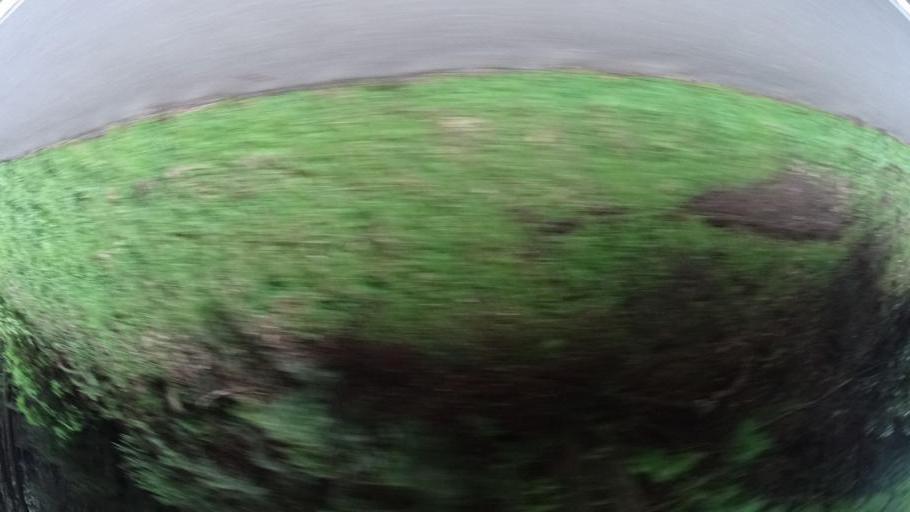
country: US
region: California
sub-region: Humboldt County
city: Rio Dell
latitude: 40.3663
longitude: -123.9230
